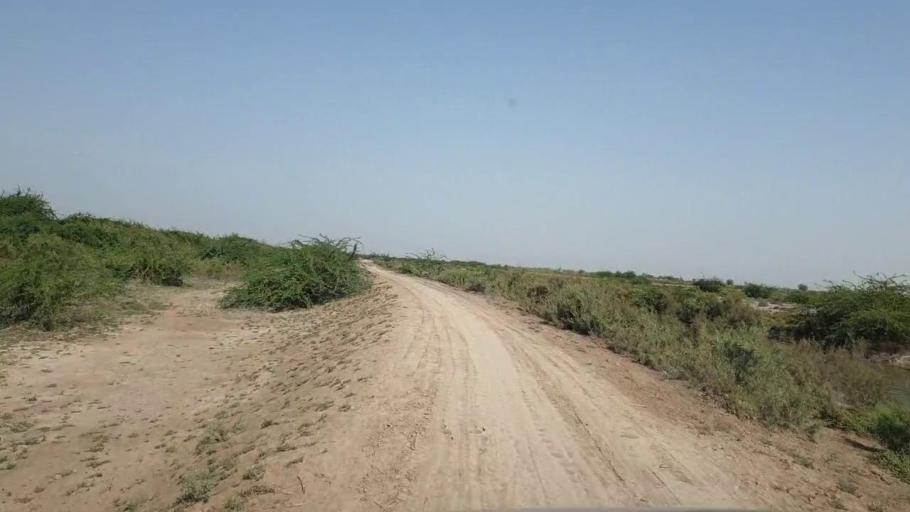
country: PK
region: Sindh
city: Tando Bago
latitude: 24.6528
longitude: 69.0706
